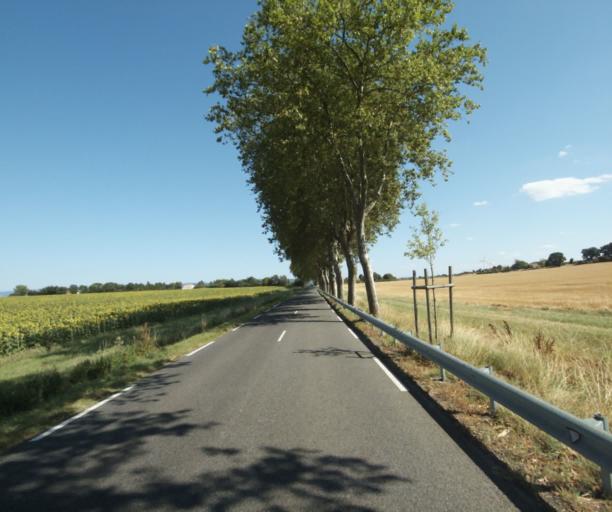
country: FR
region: Midi-Pyrenees
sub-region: Departement de la Haute-Garonne
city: Saint-Felix-Lauragais
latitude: 43.4857
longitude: 1.9101
